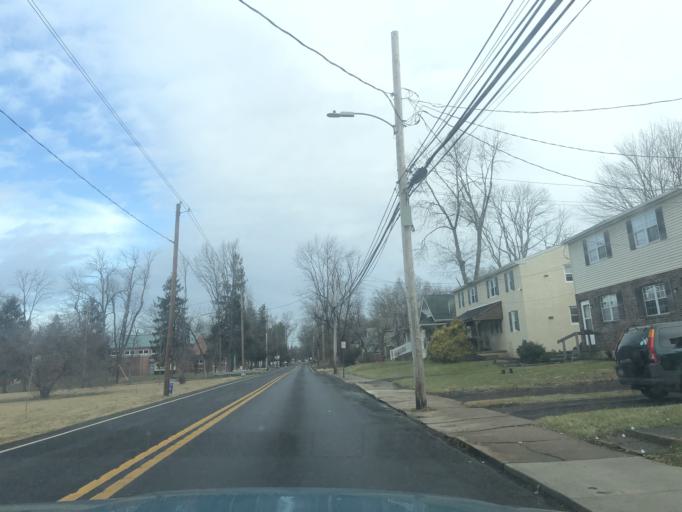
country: US
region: Pennsylvania
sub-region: Bucks County
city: Sellersville
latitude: 40.3584
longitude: -75.3051
